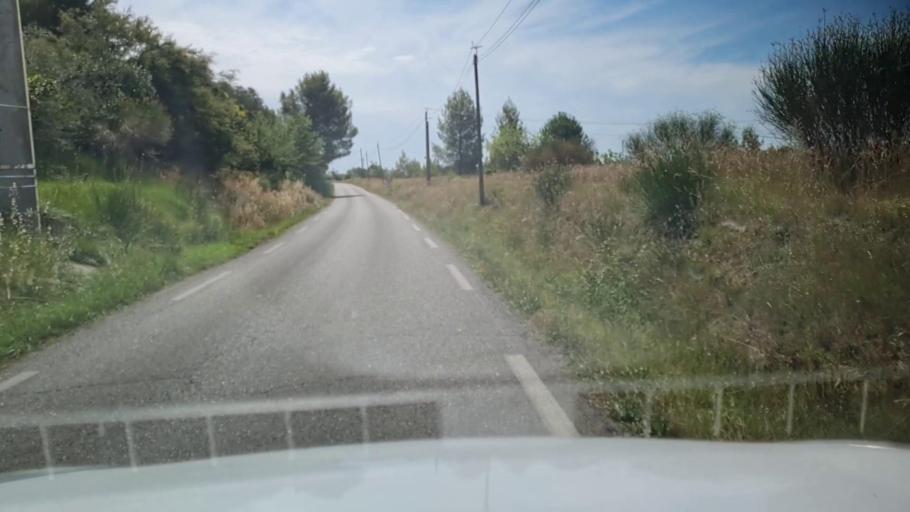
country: FR
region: Languedoc-Roussillon
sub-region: Departement du Gard
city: Nages-et-Solorgues
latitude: 43.7918
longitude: 4.2190
